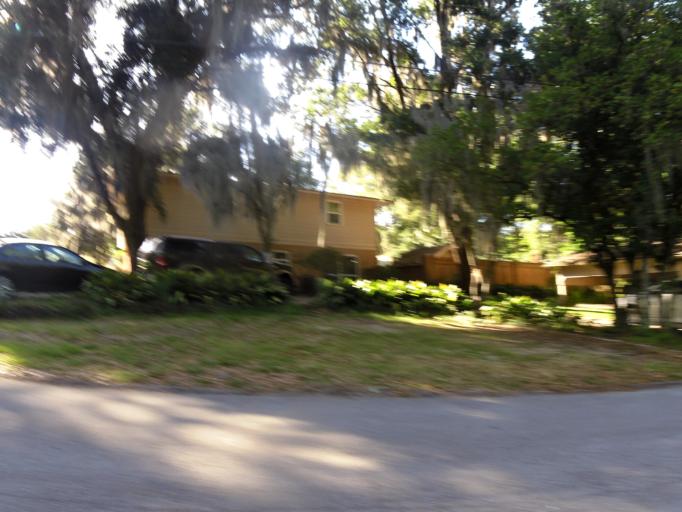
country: US
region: Florida
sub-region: Duval County
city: Jacksonville
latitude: 30.3137
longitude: -81.6164
